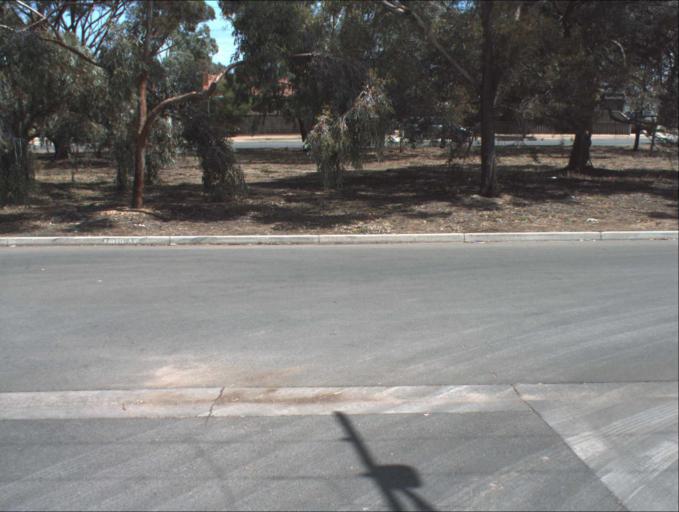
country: AU
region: South Australia
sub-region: Port Adelaide Enfield
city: Enfield
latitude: -34.8560
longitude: 138.6237
